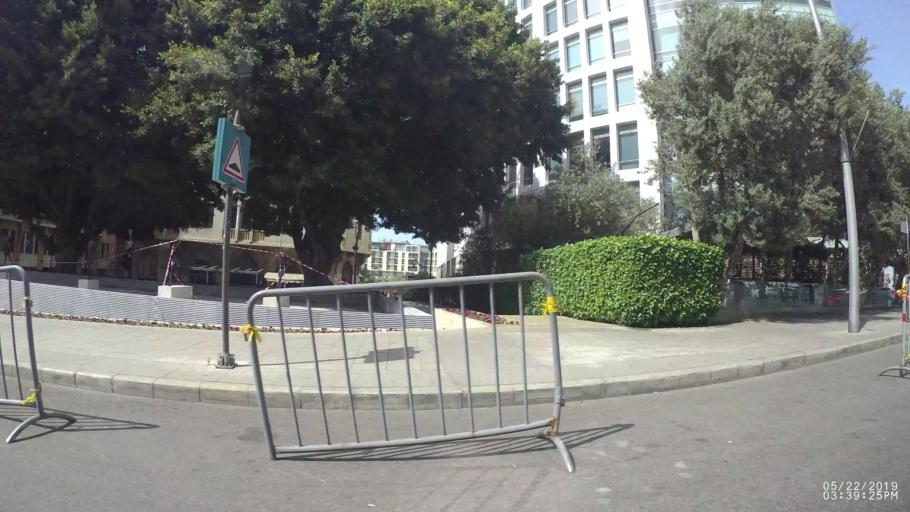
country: LB
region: Beyrouth
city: Beirut
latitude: 33.8976
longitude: 35.5068
